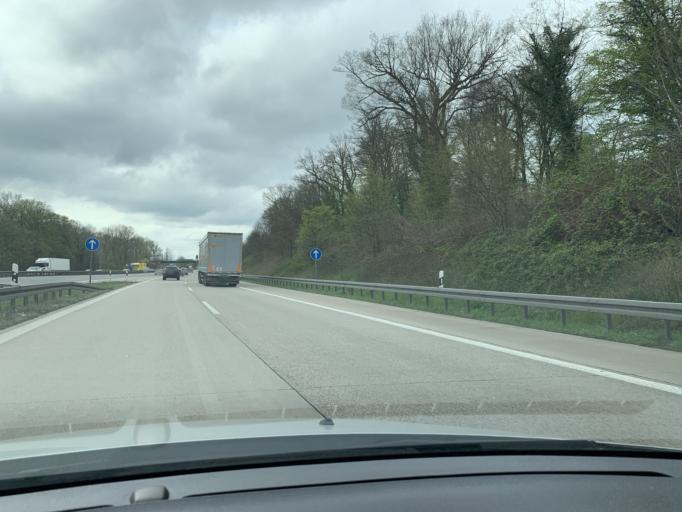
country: DE
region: Baden-Wuerttemberg
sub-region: Karlsruhe Region
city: Ettlingen
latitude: 48.9689
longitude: 8.4290
